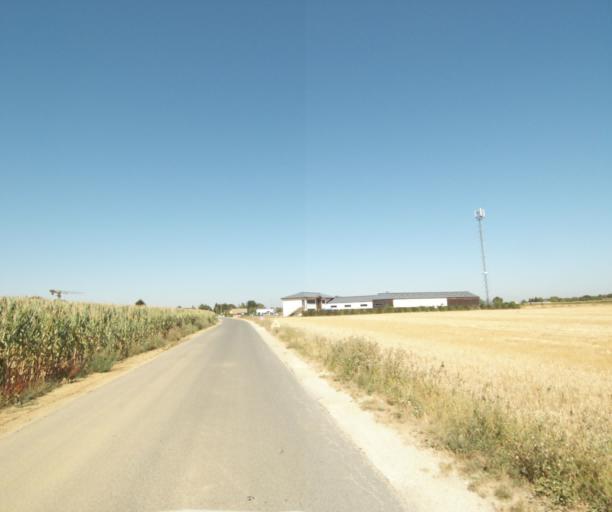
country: FR
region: Ile-de-France
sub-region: Departement de l'Essonne
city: Itteville
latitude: 48.5118
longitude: 2.3493
